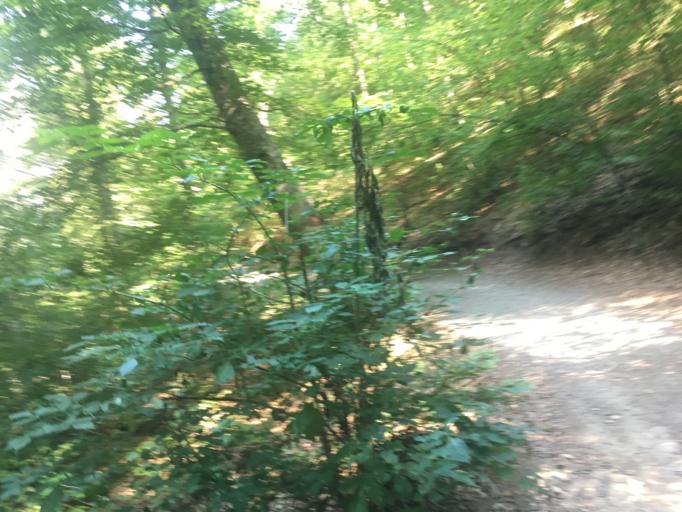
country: XK
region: Pristina
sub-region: Komuna e Prishtines
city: Pristina
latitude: 42.6628
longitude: 21.2240
